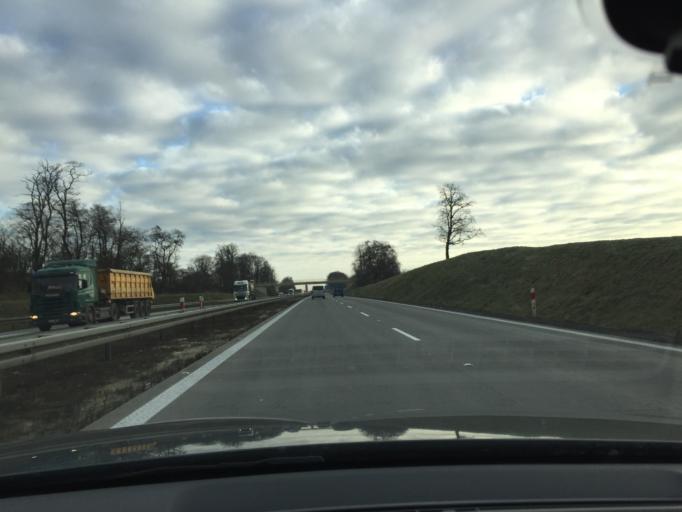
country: PL
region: Lower Silesian Voivodeship
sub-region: Powiat legnicki
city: Legnickie Pole
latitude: 51.1291
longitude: 16.3223
